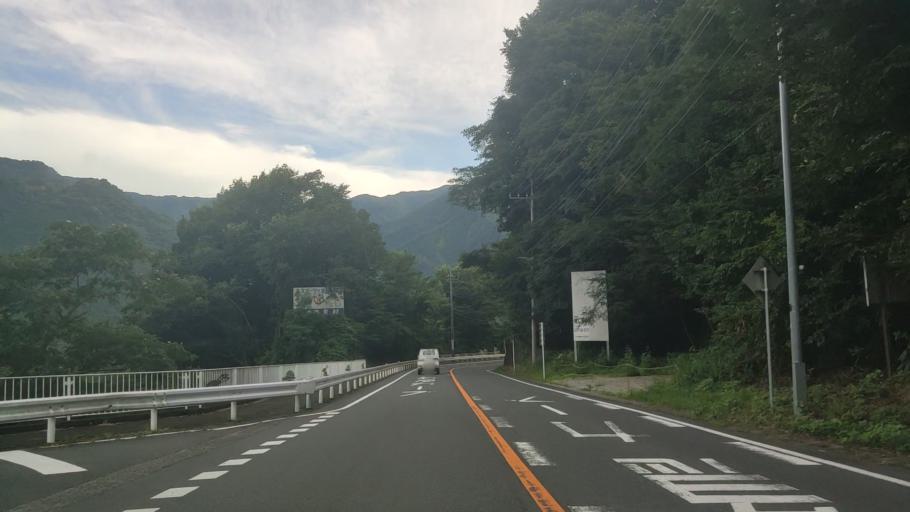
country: JP
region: Gunma
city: Omamacho-omama
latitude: 36.5421
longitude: 139.3696
